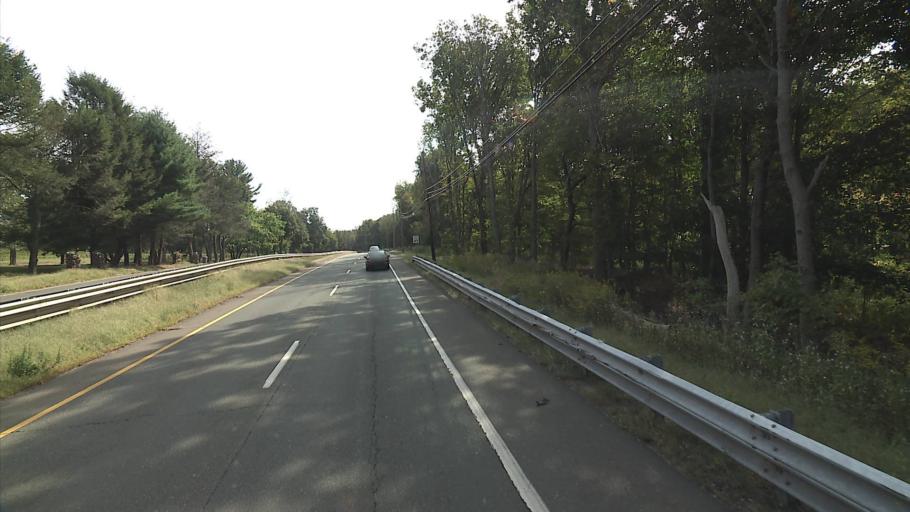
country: US
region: Connecticut
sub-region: New Haven County
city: Orange
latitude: 41.3007
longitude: -73.0234
